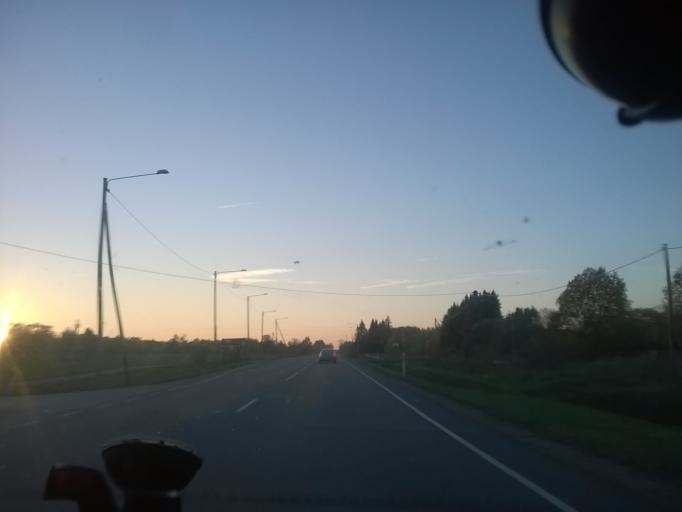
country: EE
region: Laeaene
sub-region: Ridala Parish
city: Uuemoisa
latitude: 58.9719
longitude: 23.8676
